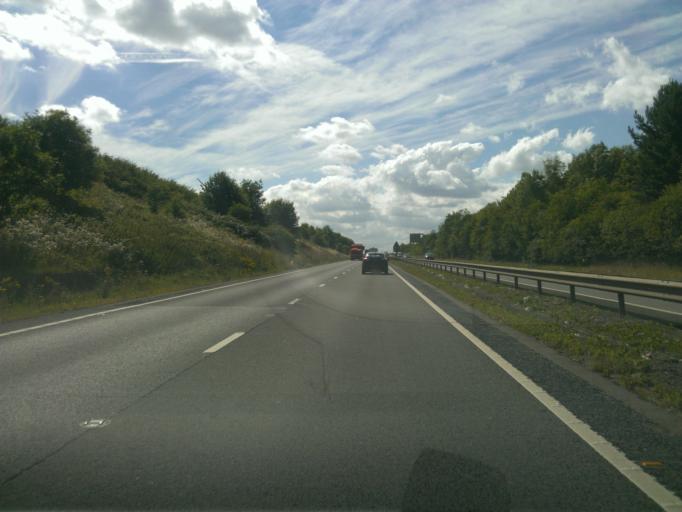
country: GB
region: England
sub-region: Northamptonshire
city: Burton Latimer
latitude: 52.3810
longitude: -0.6411
